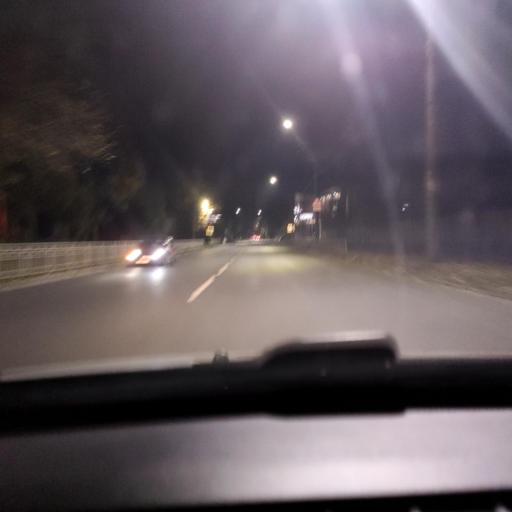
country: RU
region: Voronezj
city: Voronezh
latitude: 51.6810
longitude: 39.1937
